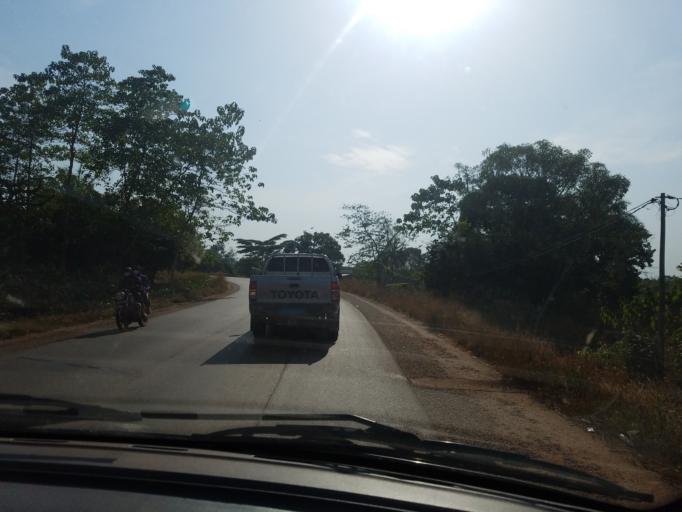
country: GN
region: Boke
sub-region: Boke Prefecture
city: Boke
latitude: 10.9088
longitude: -14.3121
